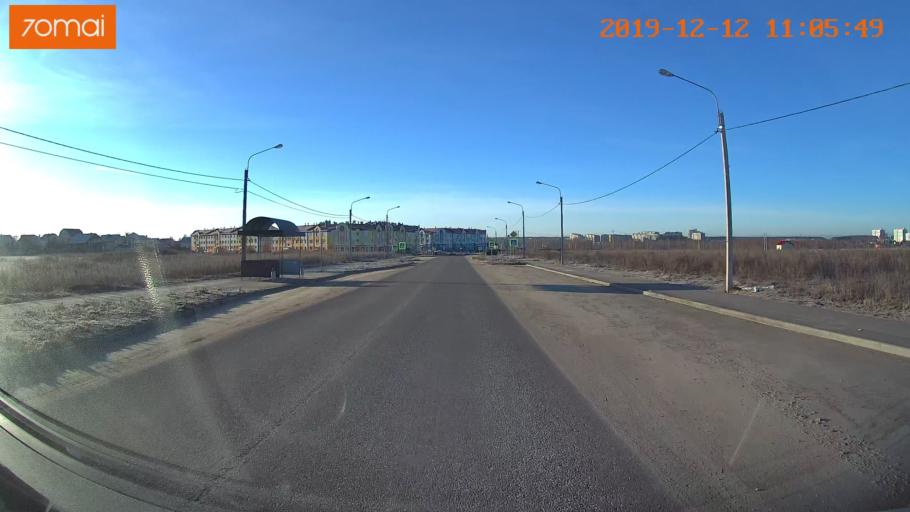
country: RU
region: Ivanovo
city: Kokhma
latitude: 56.9470
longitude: 41.0935
